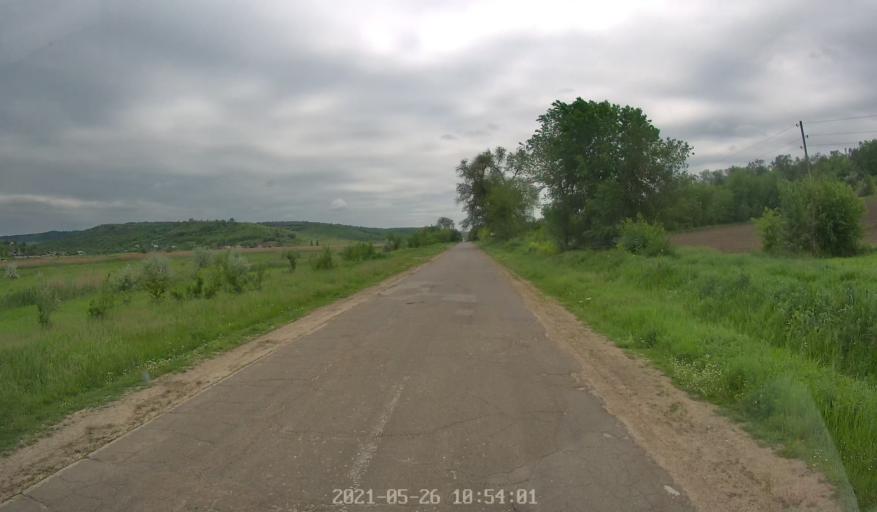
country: MD
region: Hincesti
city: Hincesti
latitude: 46.8567
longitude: 28.3908
